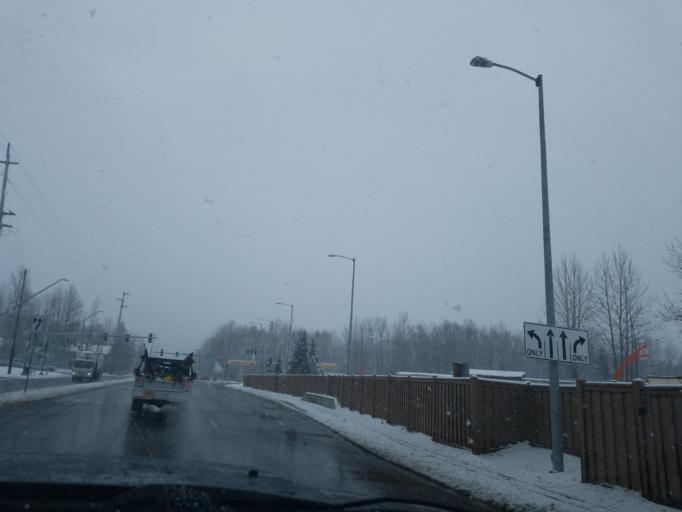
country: US
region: Alaska
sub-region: Anchorage Municipality
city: Anchorage
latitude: 61.1819
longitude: -149.8980
